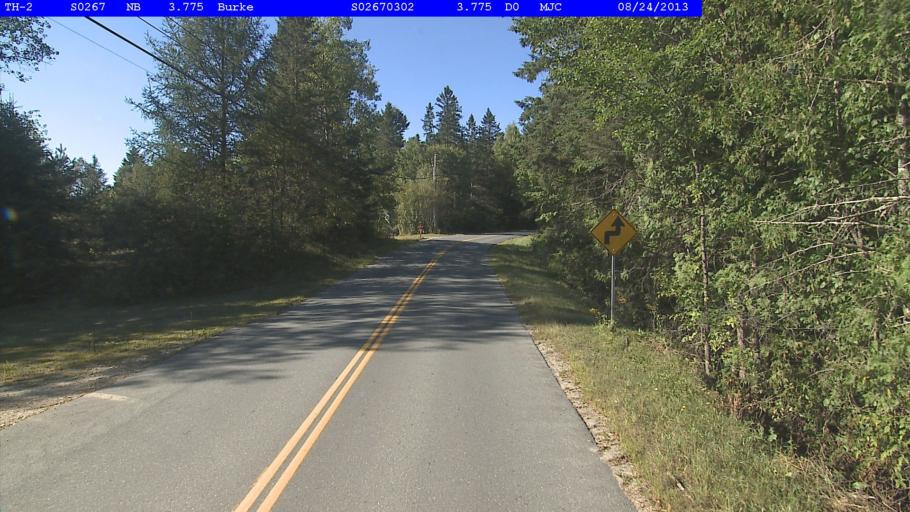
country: US
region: Vermont
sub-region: Caledonia County
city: Lyndonville
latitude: 44.6296
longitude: -71.9655
